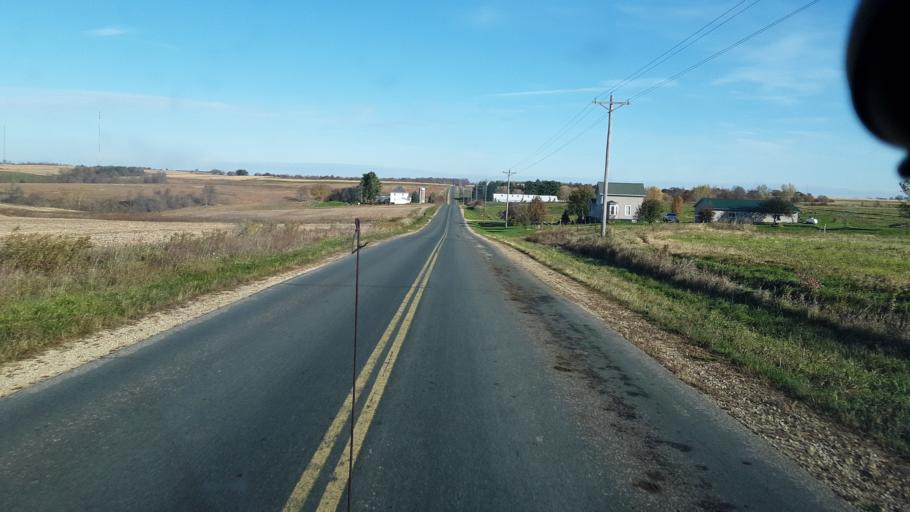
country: US
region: Wisconsin
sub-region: Vernon County
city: Hillsboro
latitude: 43.7637
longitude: -90.4331
